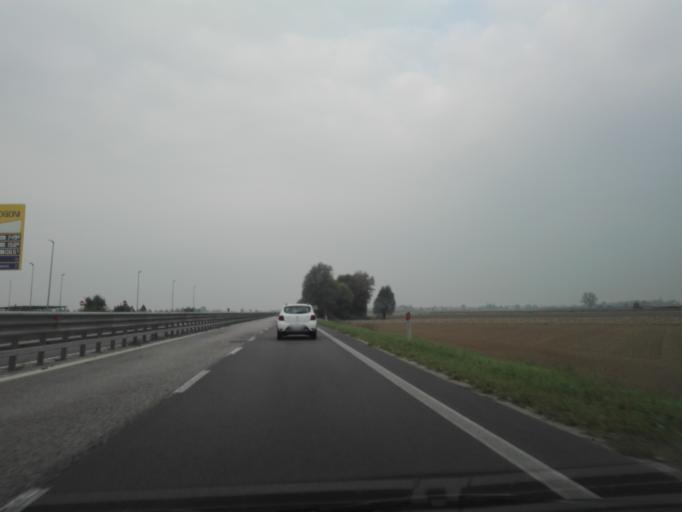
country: IT
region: Veneto
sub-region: Provincia di Verona
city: Villa Bartolomea
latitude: 45.1522
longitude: 11.3340
